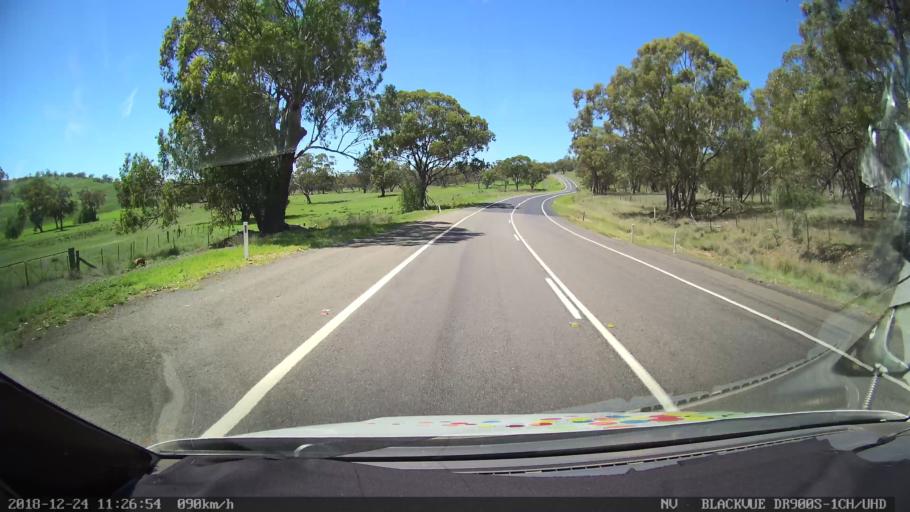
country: AU
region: New South Wales
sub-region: Upper Hunter Shire
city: Merriwa
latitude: -32.1749
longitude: 150.4336
